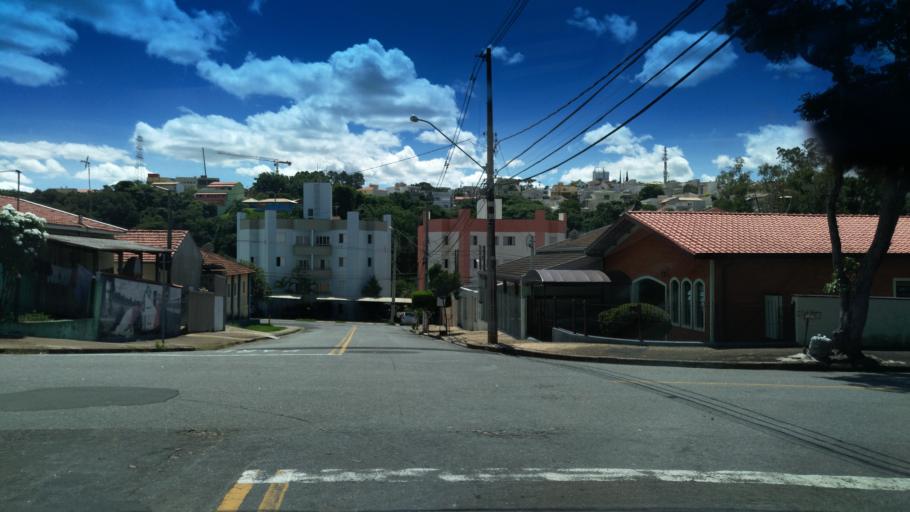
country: BR
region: Sao Paulo
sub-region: Valinhos
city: Valinhos
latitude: -22.9740
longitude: -46.9856
